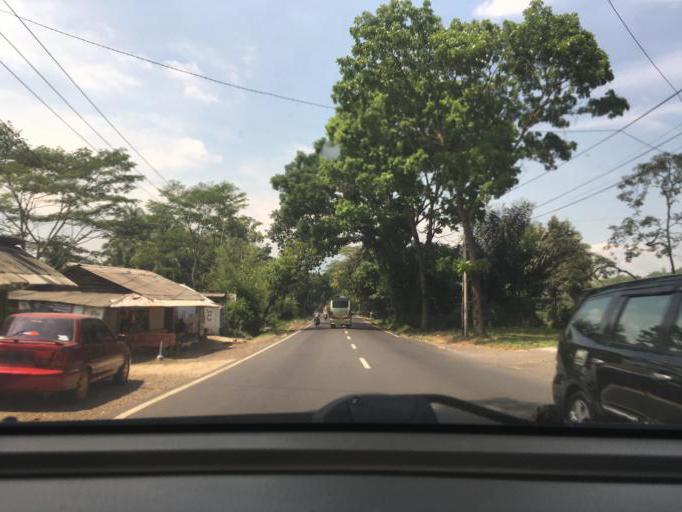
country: ID
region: West Java
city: Tagog
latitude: -7.1197
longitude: 108.1360
